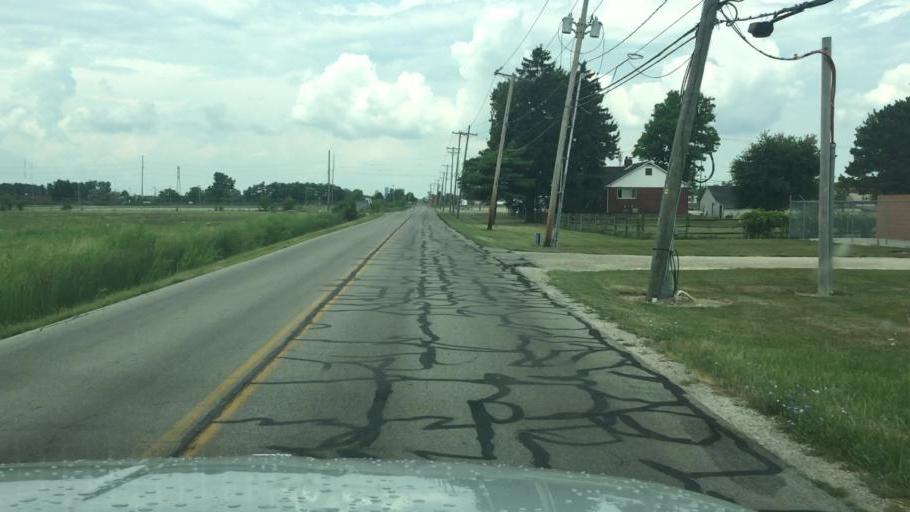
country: US
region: Ohio
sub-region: Wood County
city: Walbridge
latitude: 41.5867
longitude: -83.5279
